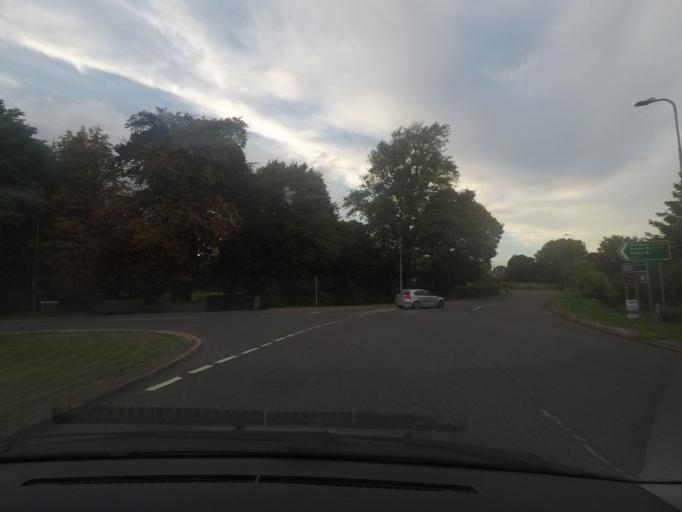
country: GB
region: England
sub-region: Lincolnshire
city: Tetney
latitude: 53.4377
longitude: -0.0522
